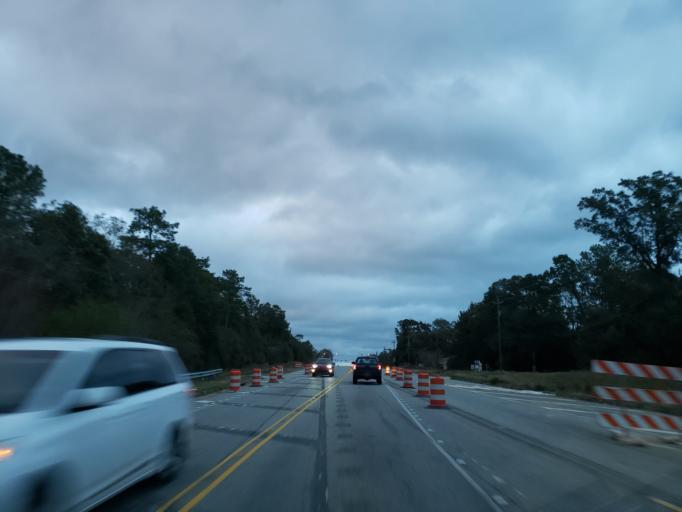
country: US
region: Alabama
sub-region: Mobile County
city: Chickasaw
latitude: 30.7890
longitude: -88.2257
